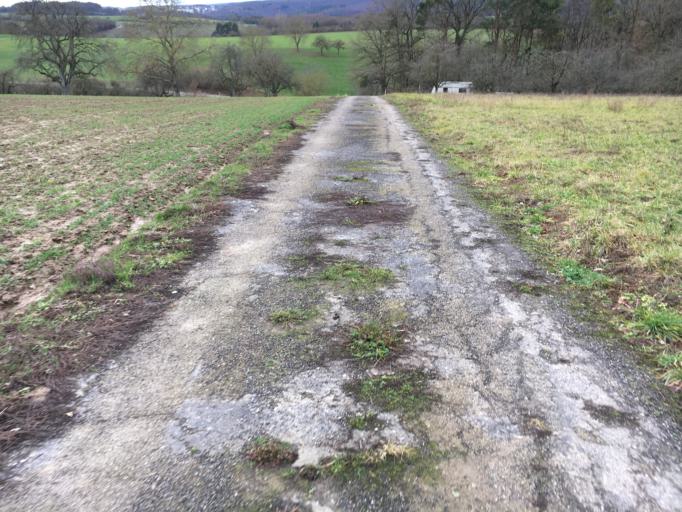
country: DE
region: Baden-Wuerttemberg
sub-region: Karlsruhe Region
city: Mosbach
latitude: 49.3744
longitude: 9.1970
